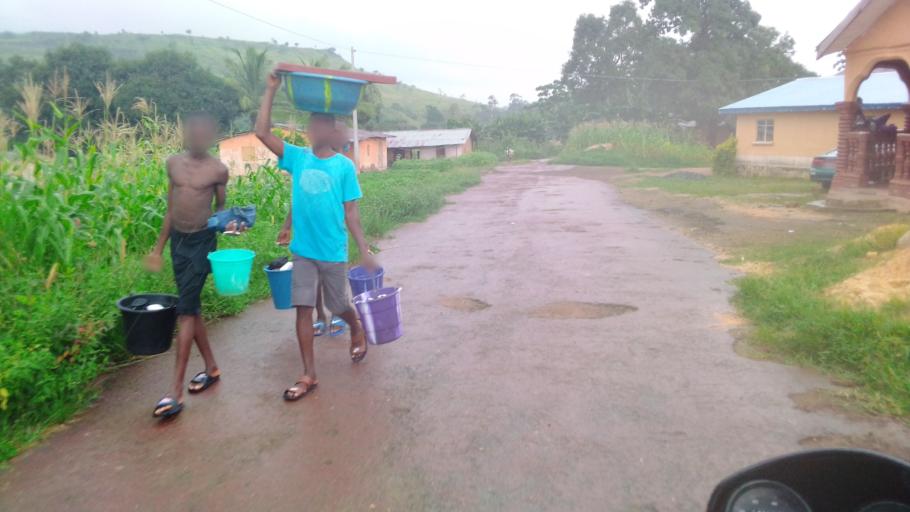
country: SL
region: Northern Province
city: Lunsar
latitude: 8.6821
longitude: -12.5282
